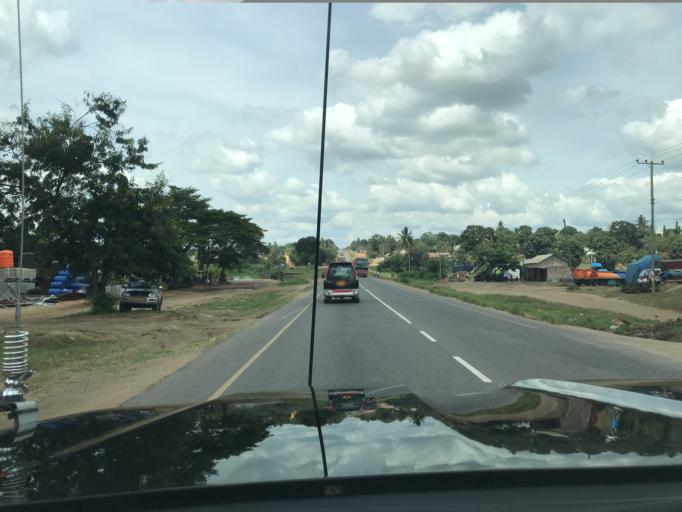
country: TZ
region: Pwani
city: Kibaha
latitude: -6.7636
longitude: 38.9503
